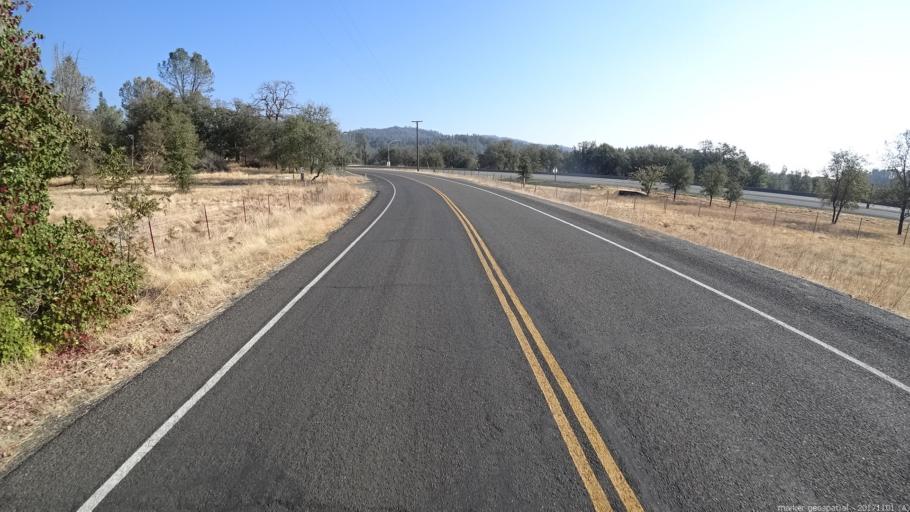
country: US
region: California
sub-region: Shasta County
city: Shasta Lake
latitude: 40.7080
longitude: -122.3370
